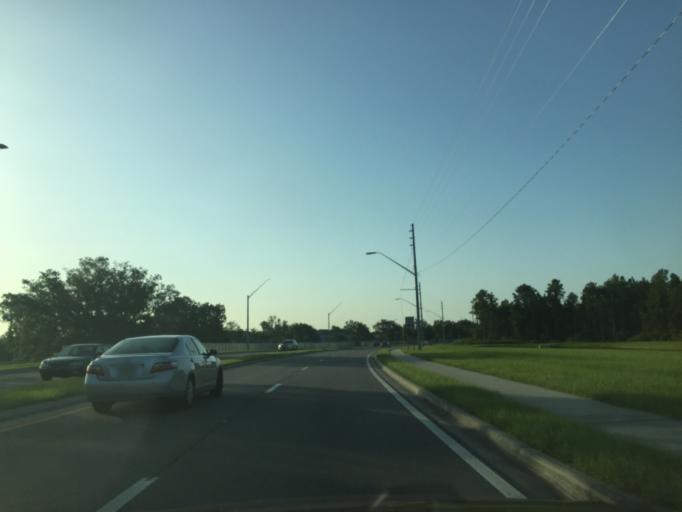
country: US
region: Florida
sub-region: Orange County
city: Alafaya
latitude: 28.5239
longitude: -81.1918
